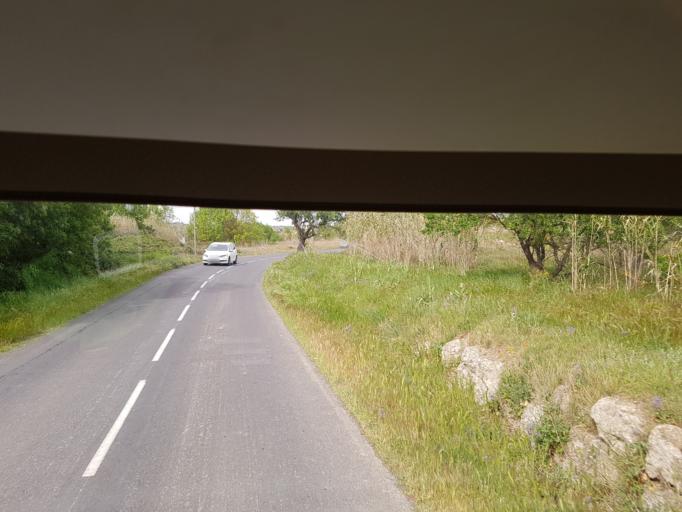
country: FR
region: Languedoc-Roussillon
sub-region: Departement de l'Herault
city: Lespignan
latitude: 43.2602
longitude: 3.1605
